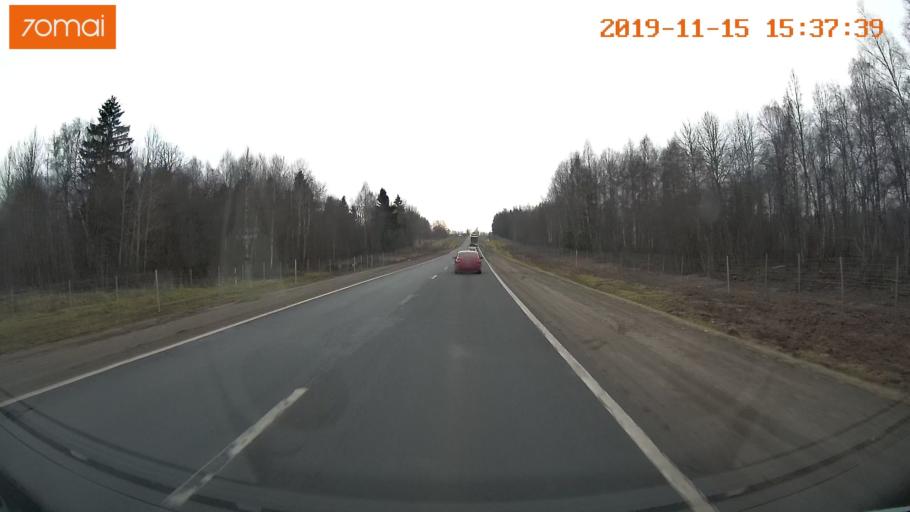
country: RU
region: Jaroslavl
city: Danilov
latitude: 58.0373
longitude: 40.0875
